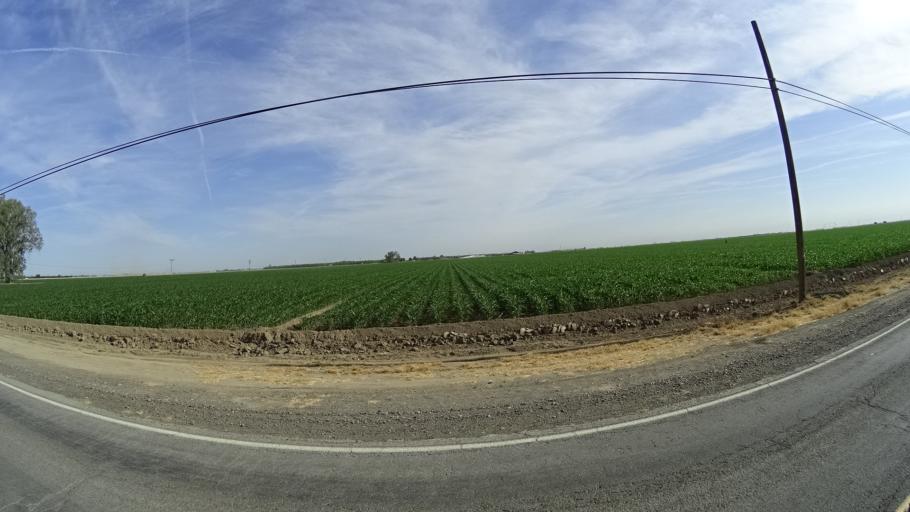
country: US
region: California
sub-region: Kings County
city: Home Garden
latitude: 36.3428
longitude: -119.5454
